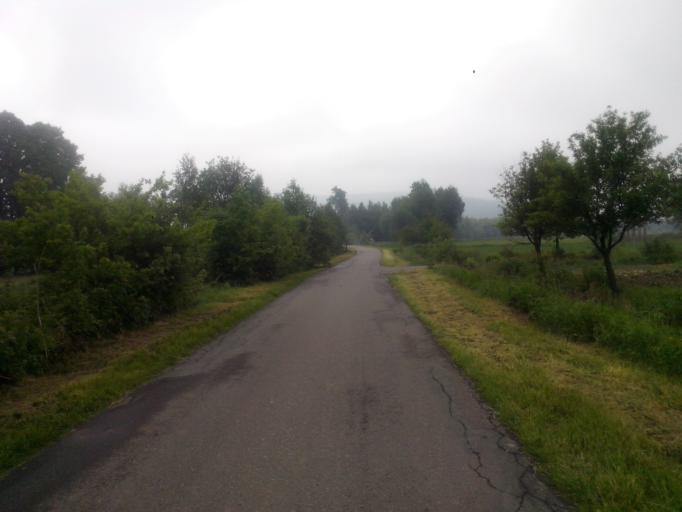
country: PL
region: Subcarpathian Voivodeship
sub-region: Powiat strzyzowski
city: Wysoka Strzyzowska
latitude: 49.8087
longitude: 21.7819
